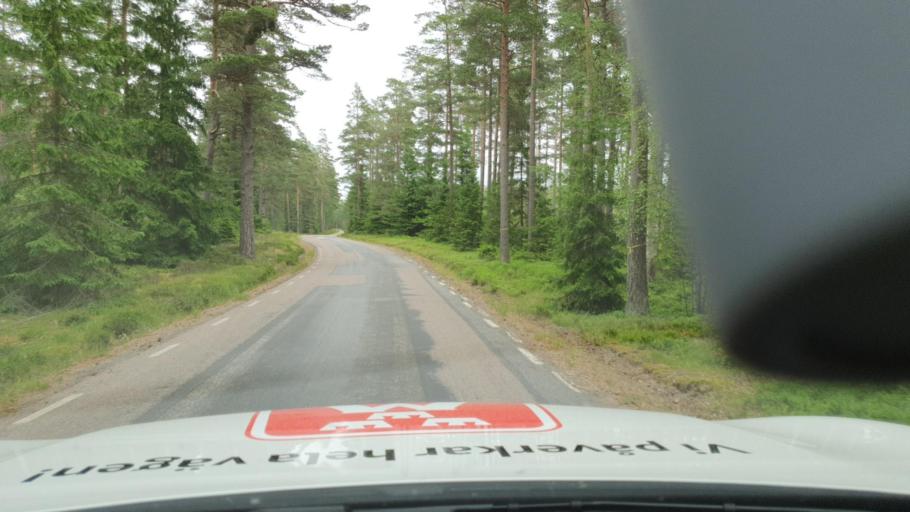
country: SE
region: Vaestra Goetaland
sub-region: Karlsborgs Kommun
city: Molltorp
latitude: 58.4136
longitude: 14.3288
